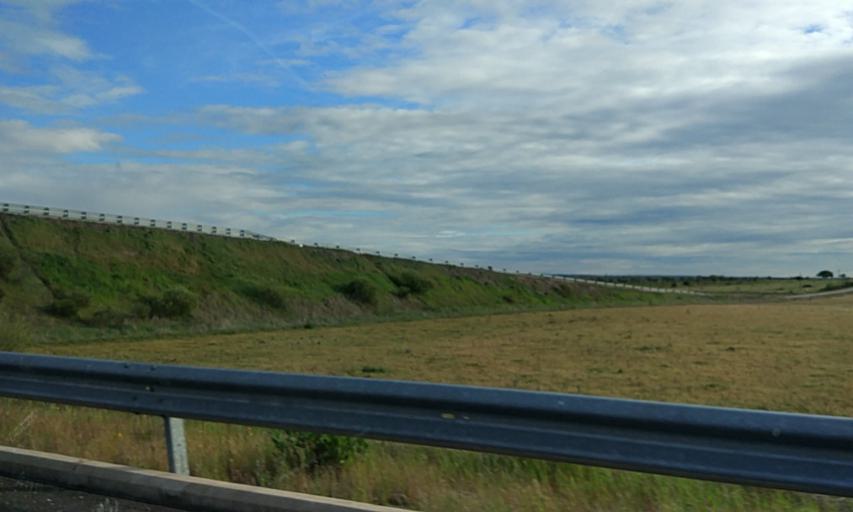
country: ES
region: Extremadura
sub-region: Provincia de Caceres
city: Casas de Don Gomez
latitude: 40.0166
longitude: -6.5868
